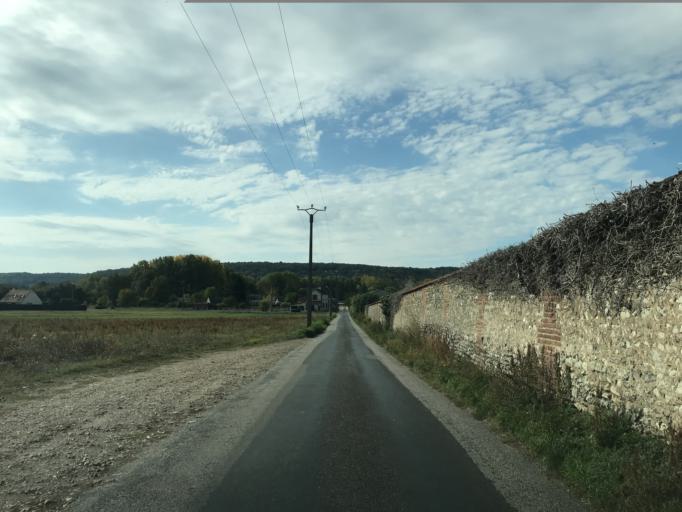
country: FR
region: Haute-Normandie
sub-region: Departement de l'Eure
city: Saint-Aubin-sur-Gaillon
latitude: 49.0921
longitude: 1.2849
